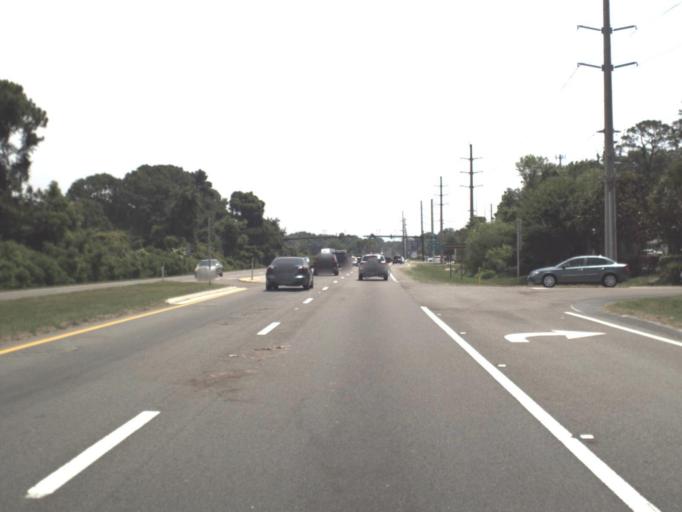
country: US
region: Florida
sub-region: Nassau County
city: Fernandina Beach
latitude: 30.6309
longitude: -81.4730
